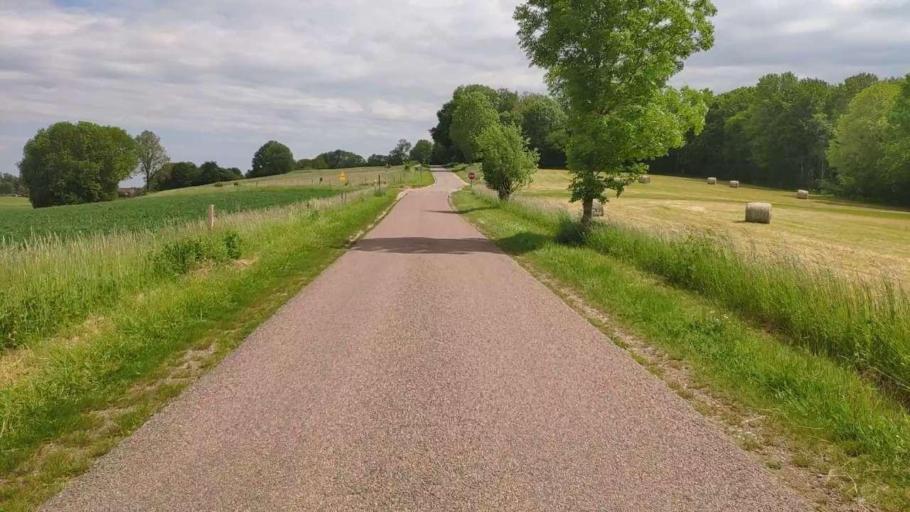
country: FR
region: Franche-Comte
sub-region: Departement du Jura
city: Poligny
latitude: 46.7801
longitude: 5.6634
